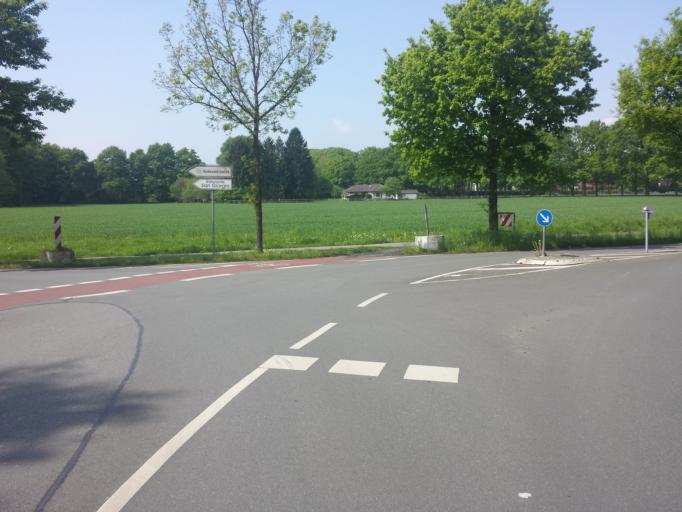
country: DE
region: North Rhine-Westphalia
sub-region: Regierungsbezirk Detmold
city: Guetersloh
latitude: 51.8940
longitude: 8.3960
